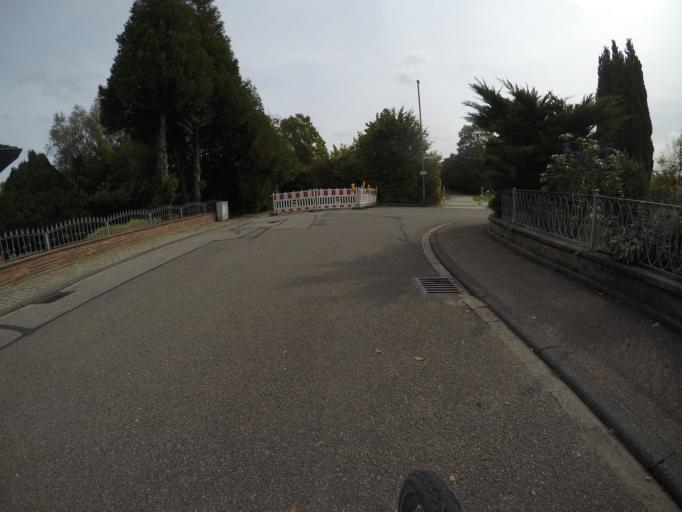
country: DE
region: Baden-Wuerttemberg
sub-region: Karlsruhe Region
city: Ubstadt-Weiher
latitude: 49.1643
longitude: 8.6344
